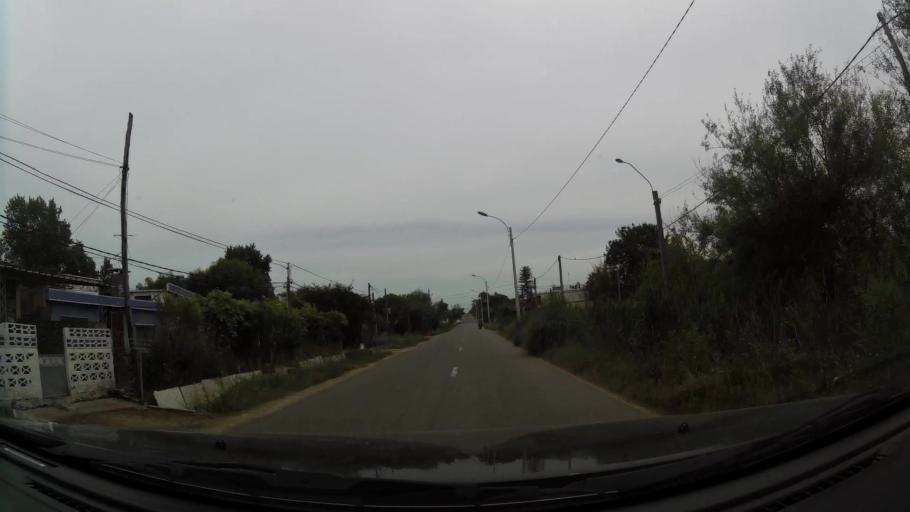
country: UY
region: Canelones
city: Las Piedras
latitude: -34.7411
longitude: -56.2314
